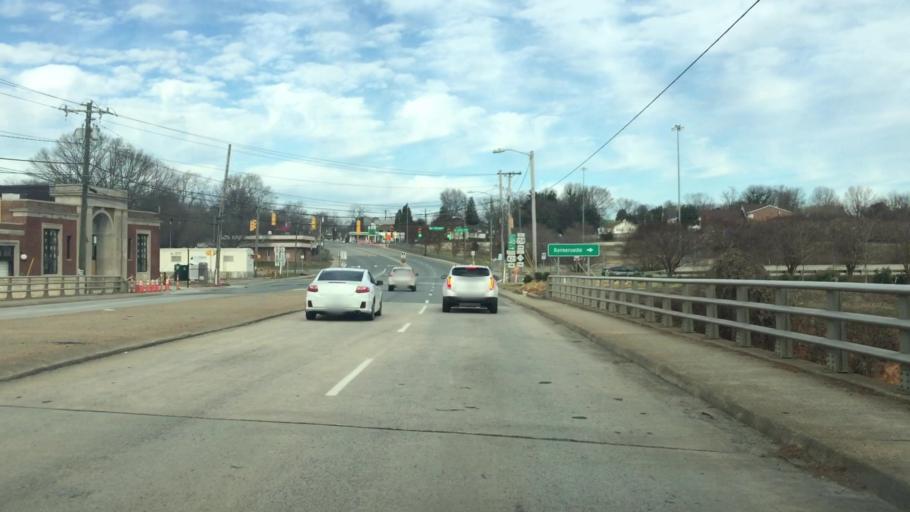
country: US
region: North Carolina
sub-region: Forsyth County
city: Winston-Salem
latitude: 36.0930
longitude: -80.2276
